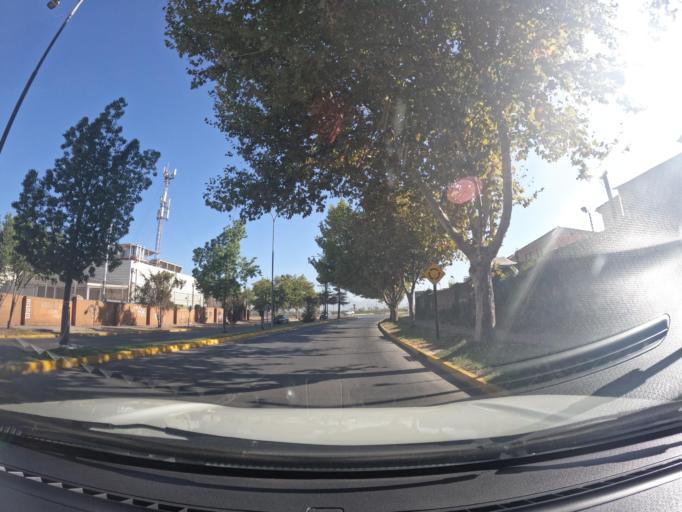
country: CL
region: Santiago Metropolitan
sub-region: Provincia de Santiago
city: Villa Presidente Frei, Nunoa, Santiago, Chile
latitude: -33.4862
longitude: -70.5768
